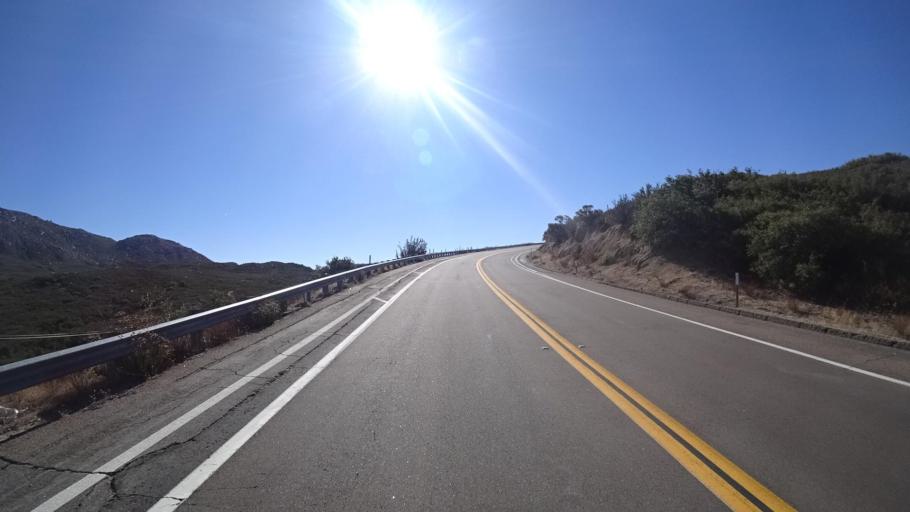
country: US
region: California
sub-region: San Diego County
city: Descanso
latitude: 32.8407
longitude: -116.6818
